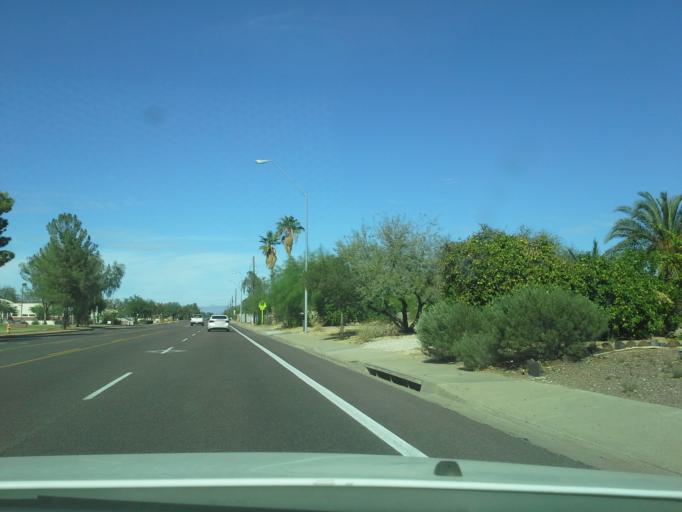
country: US
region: Arizona
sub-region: Maricopa County
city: Paradise Valley
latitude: 33.6315
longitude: -111.9958
